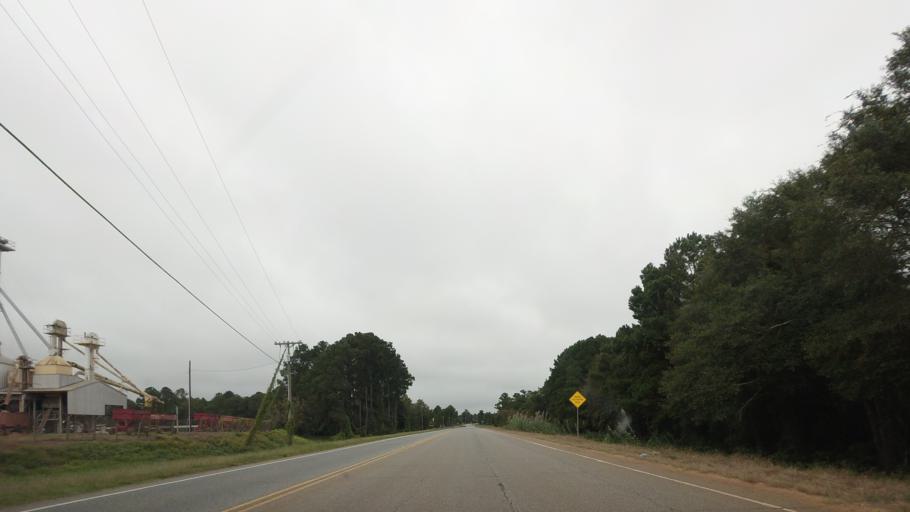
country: US
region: Georgia
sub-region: Irwin County
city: Ocilla
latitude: 31.6472
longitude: -83.2456
